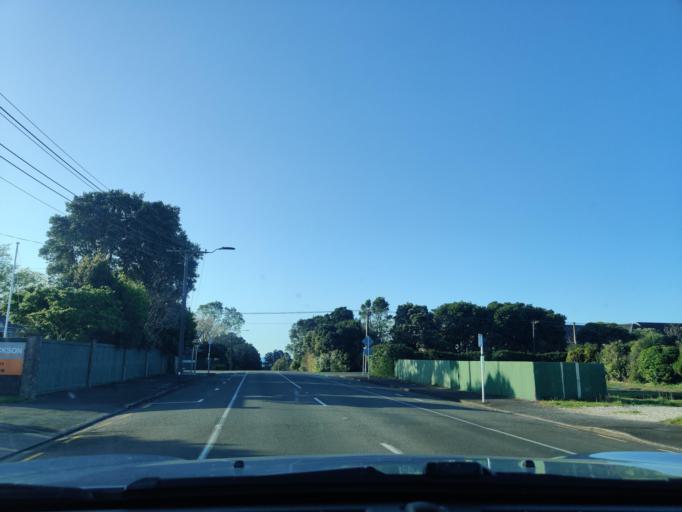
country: NZ
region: Taranaki
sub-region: New Plymouth District
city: New Plymouth
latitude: -39.0667
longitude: 174.0658
